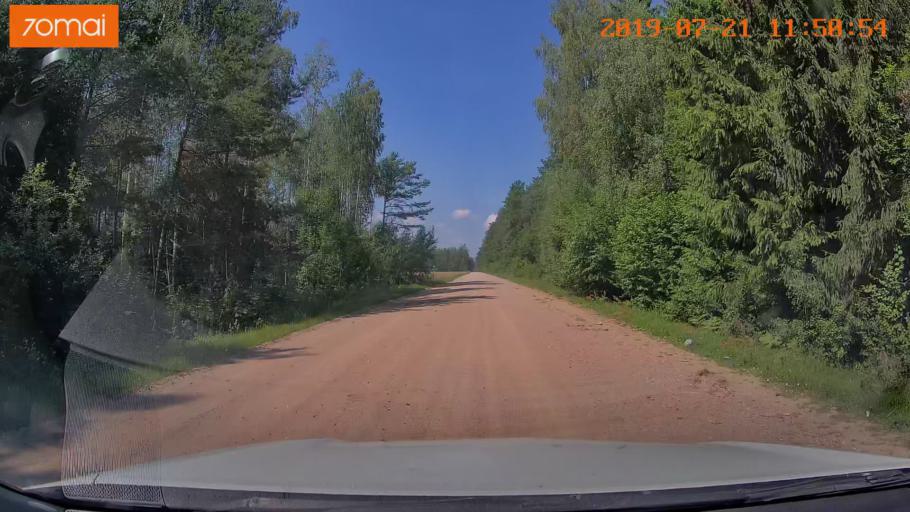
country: BY
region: Grodnenskaya
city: Lyubcha
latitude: 53.8850
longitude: 26.0186
